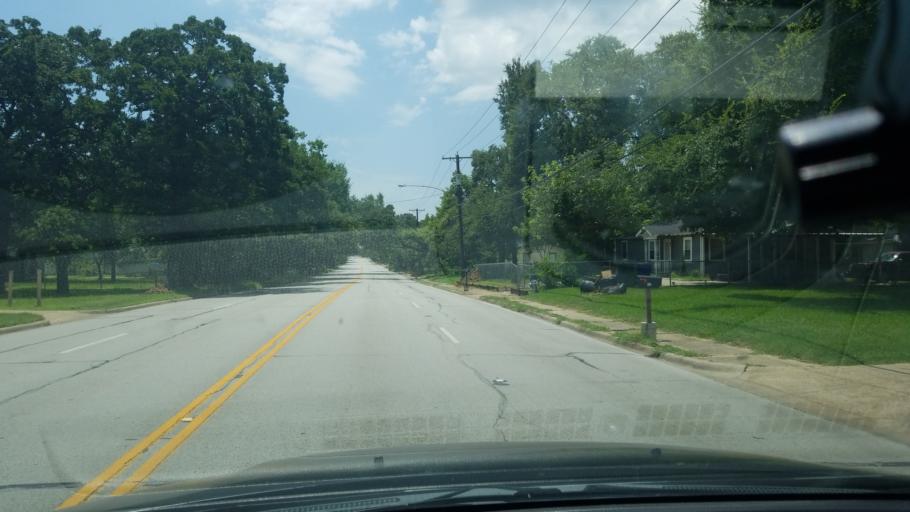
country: US
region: Texas
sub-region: Dallas County
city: Balch Springs
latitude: 32.7182
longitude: -96.6571
